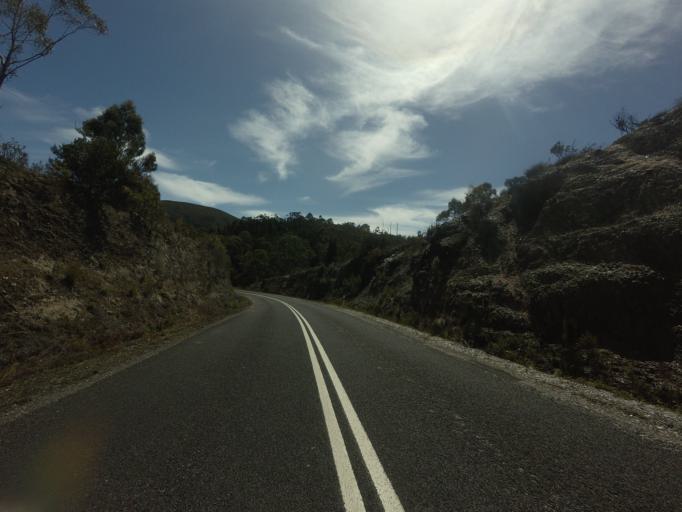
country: AU
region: Tasmania
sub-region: West Coast
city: Queenstown
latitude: -42.7988
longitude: 146.0905
